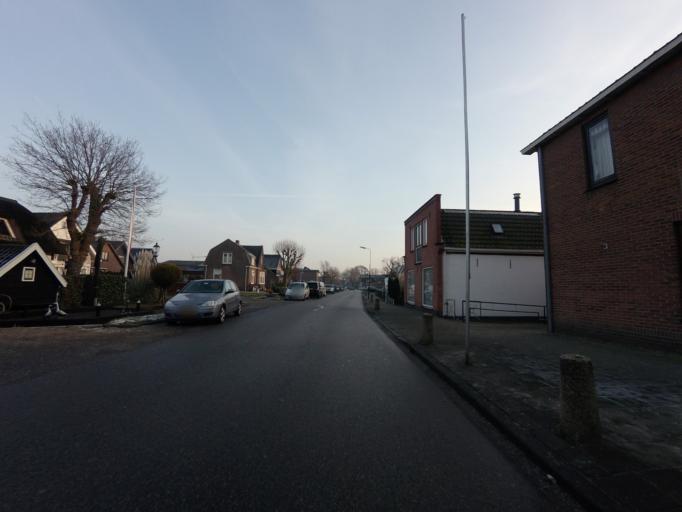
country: NL
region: Utrecht
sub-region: Gemeente De Ronde Venen
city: Mijdrecht
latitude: 52.2212
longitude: 4.9313
